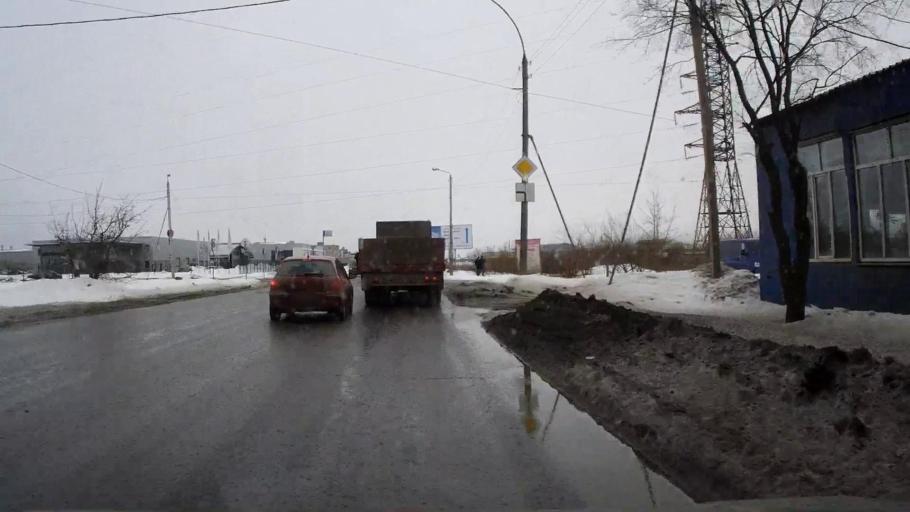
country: RU
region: Vologda
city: Vologda
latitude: 59.2189
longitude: 39.9424
